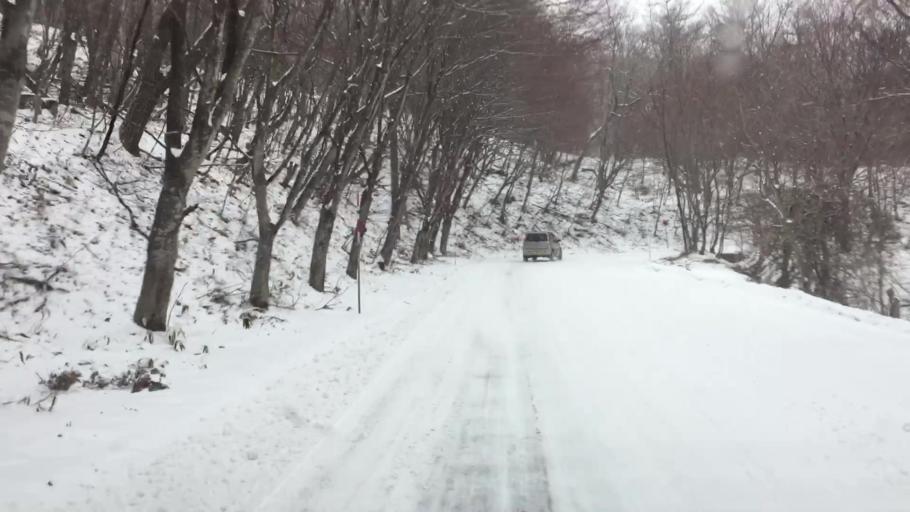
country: JP
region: Tochigi
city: Imaichi
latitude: 36.8856
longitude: 139.7355
